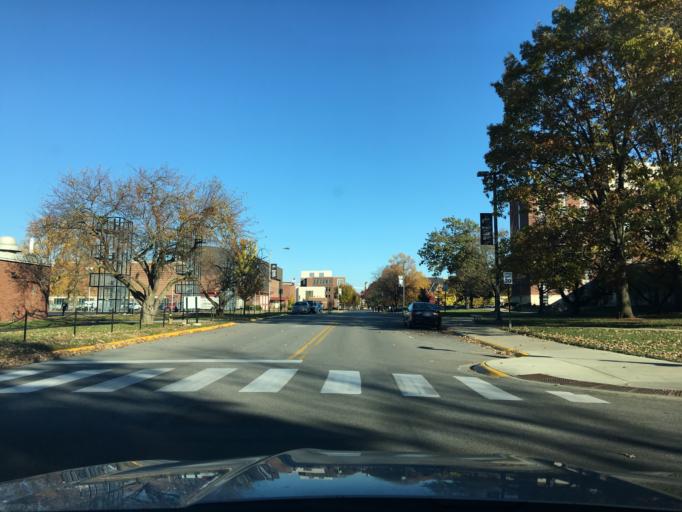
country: US
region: Indiana
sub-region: Tippecanoe County
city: West Lafayette
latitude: 40.4274
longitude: -86.9258
